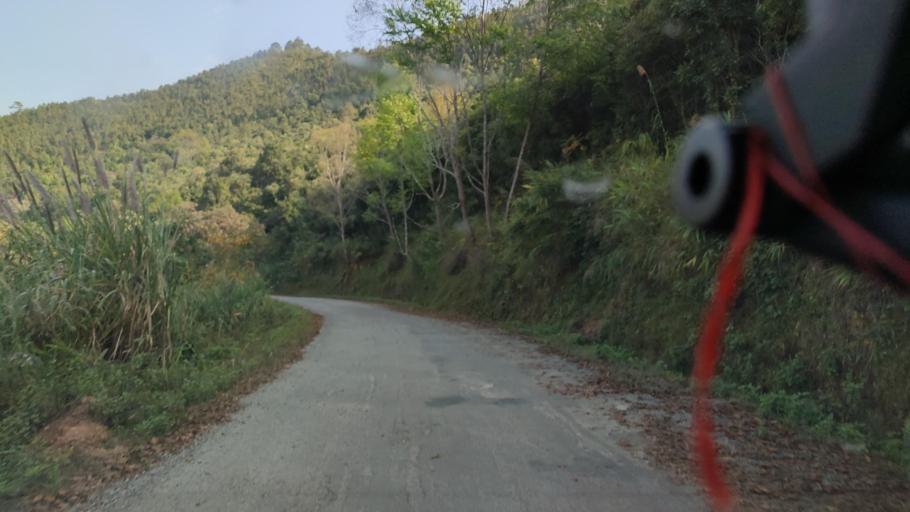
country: CN
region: Yunnan
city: Menghai
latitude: 21.4569
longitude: 99.7043
